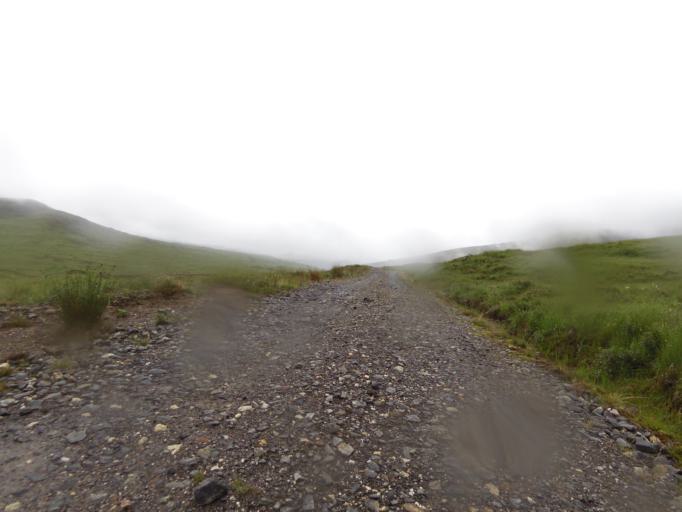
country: GB
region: Scotland
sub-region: Highland
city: Spean Bridge
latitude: 56.7698
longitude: -4.6956
